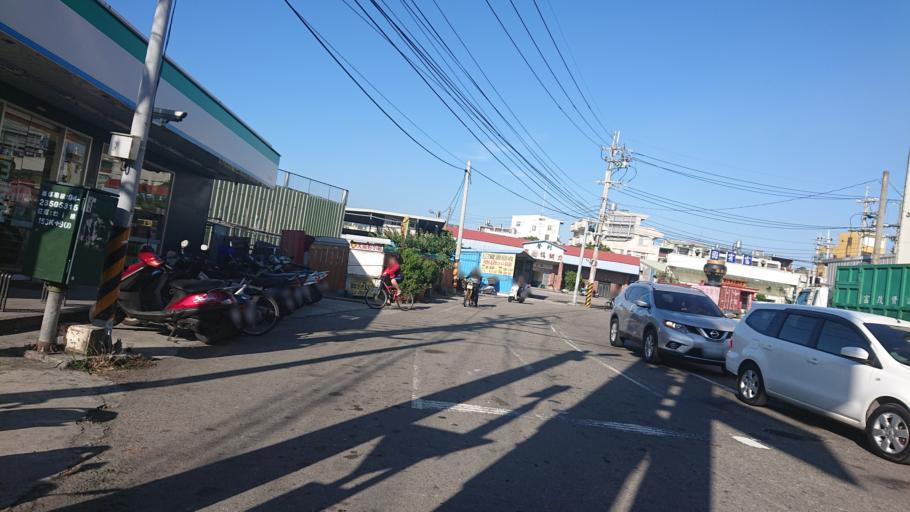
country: TW
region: Taiwan
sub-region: Changhua
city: Chang-hua
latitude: 24.1190
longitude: 120.5764
